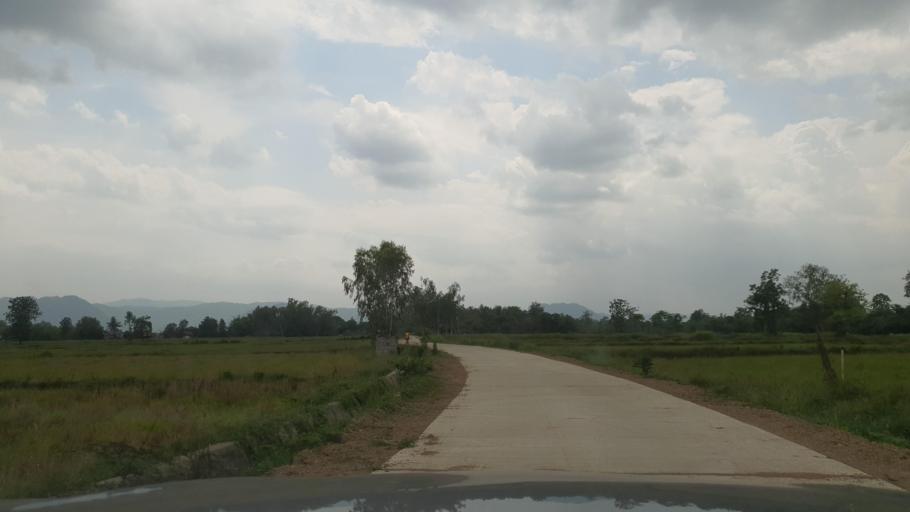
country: TH
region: Sukhothai
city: Thung Saliam
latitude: 17.3303
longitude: 99.4443
